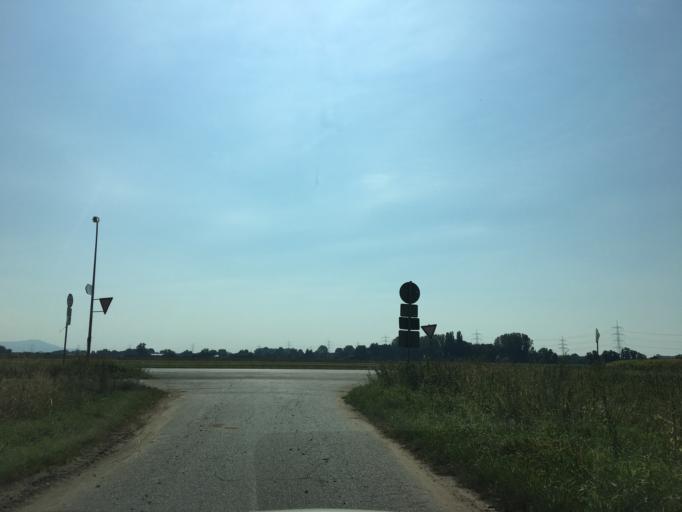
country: DE
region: Hesse
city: Griesheim
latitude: 49.8587
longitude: 8.5407
